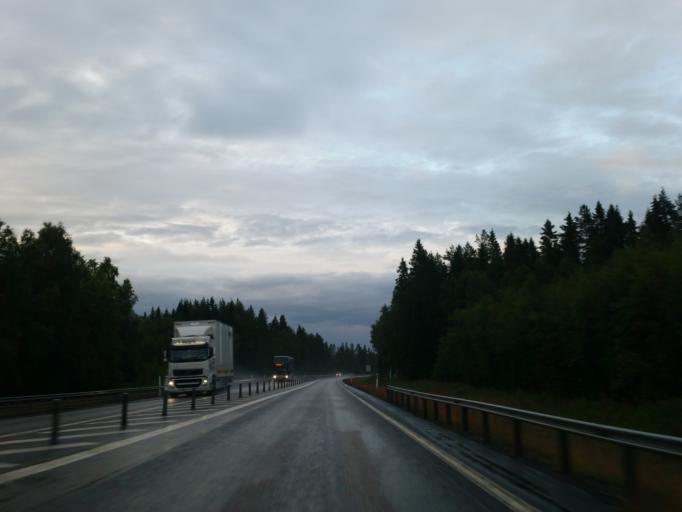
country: SE
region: Vaesterbotten
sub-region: Umea Kommun
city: Saevar
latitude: 63.9144
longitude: 20.5950
